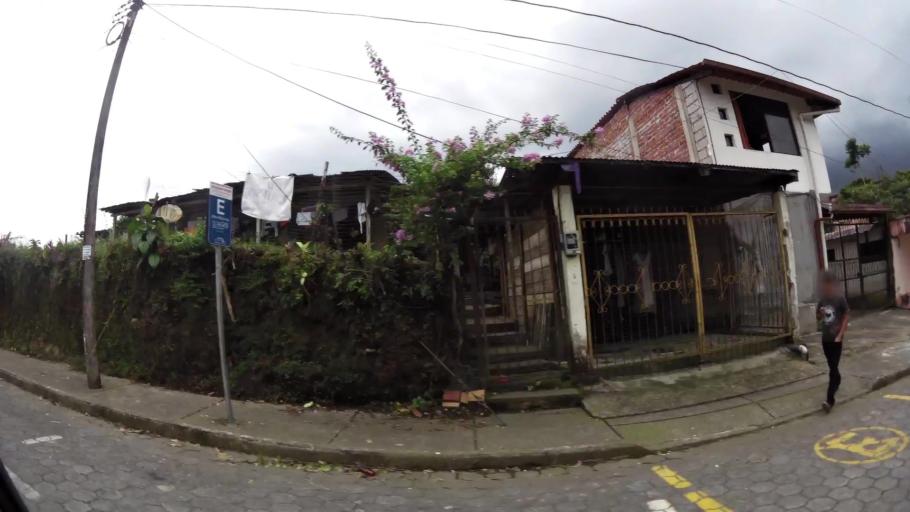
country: EC
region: Pastaza
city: Puyo
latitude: -1.4880
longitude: -77.9932
